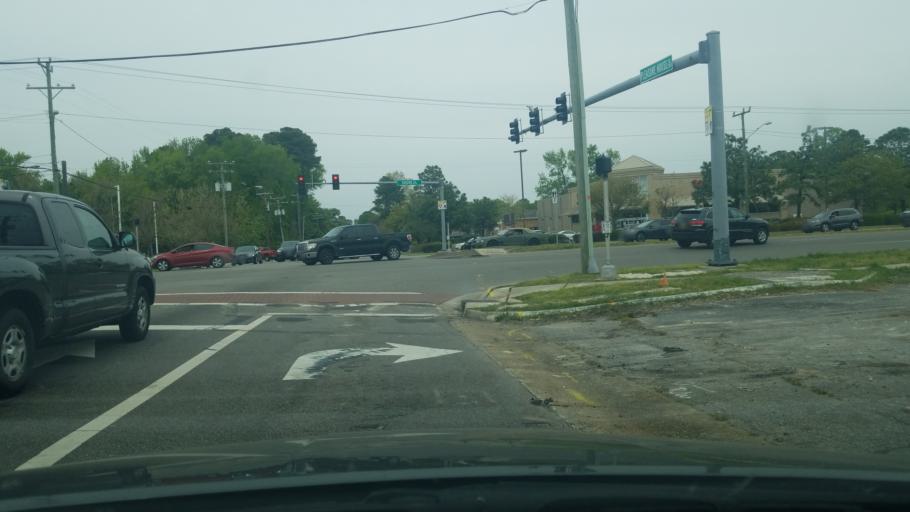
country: US
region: Virginia
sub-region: City of Norfolk
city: Norfolk
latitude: 36.9041
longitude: -76.1357
